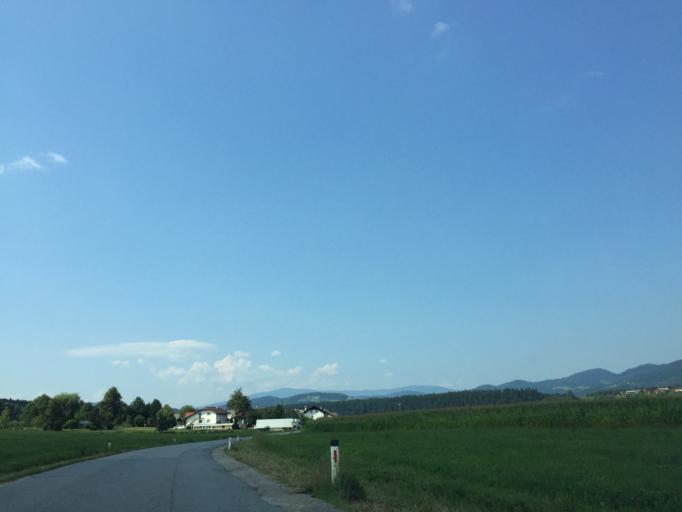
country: SI
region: Slovenj Gradec
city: Smartno pri Slovenj Gradcu
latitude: 46.4728
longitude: 15.0831
